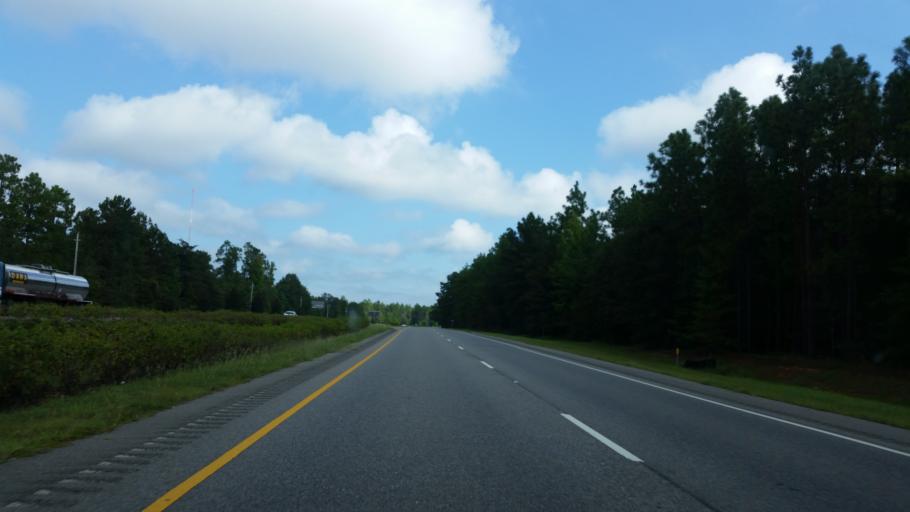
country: US
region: Alabama
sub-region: Baldwin County
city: Bay Minette
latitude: 30.9307
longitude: -87.7691
